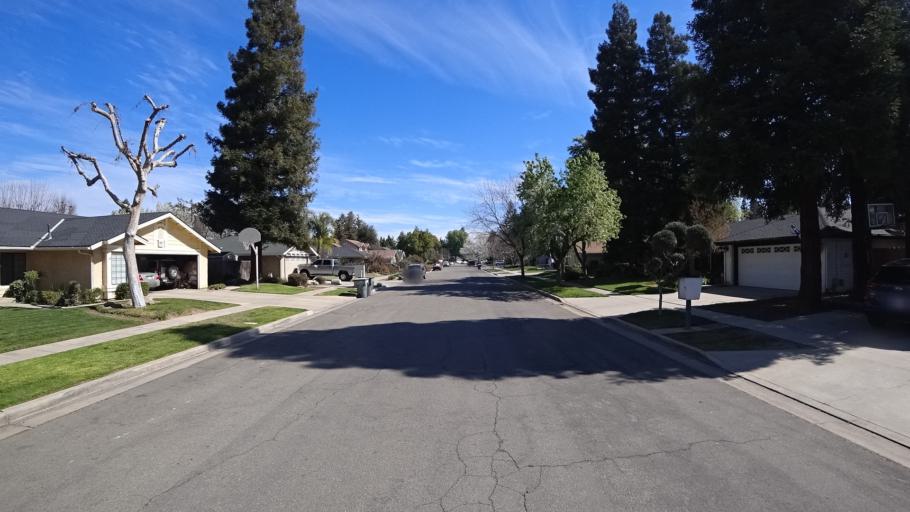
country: US
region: California
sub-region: Fresno County
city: Clovis
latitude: 36.8572
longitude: -119.7648
